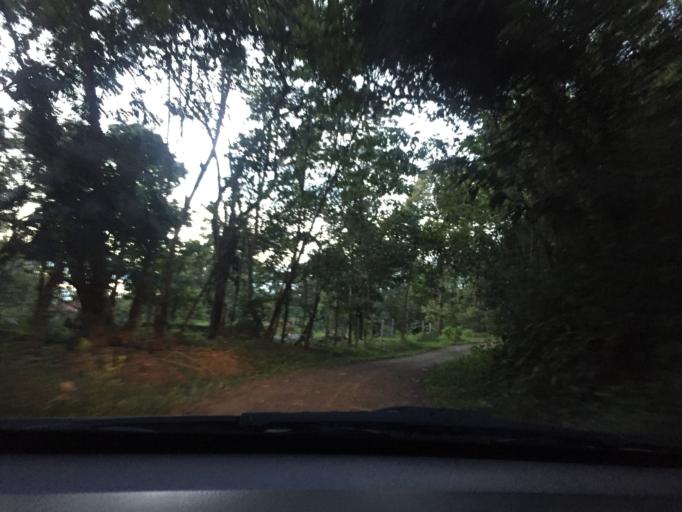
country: CO
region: Cundinamarca
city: Zipacon
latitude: 4.7110
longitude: -74.4100
